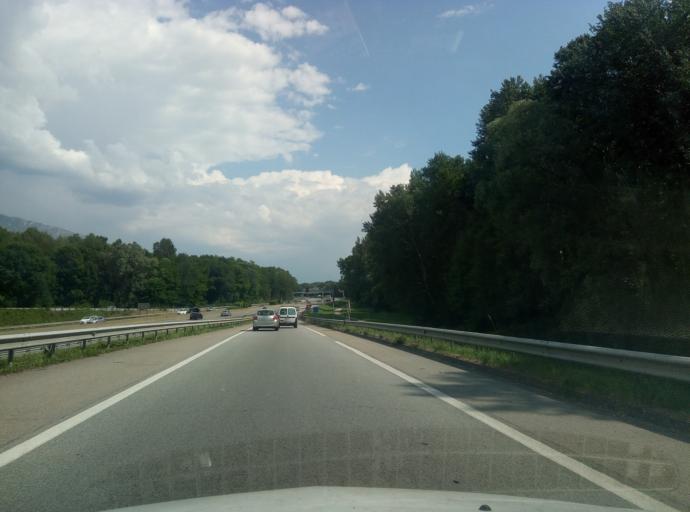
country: FR
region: Rhone-Alpes
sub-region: Departement de l'Isere
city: Veurey-Voroize
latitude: 45.2717
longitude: 5.6256
